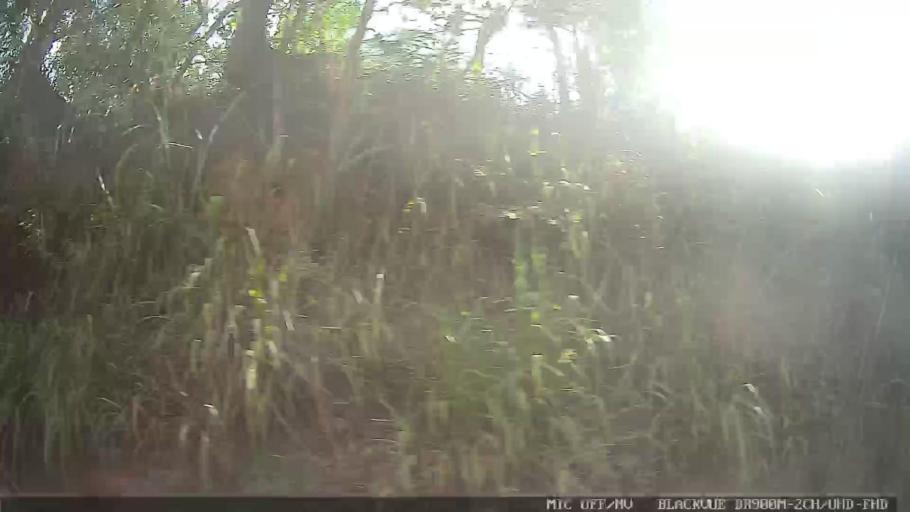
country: BR
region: Sao Paulo
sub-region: Bom Jesus Dos Perdoes
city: Bom Jesus dos Perdoes
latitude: -23.1196
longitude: -46.5025
